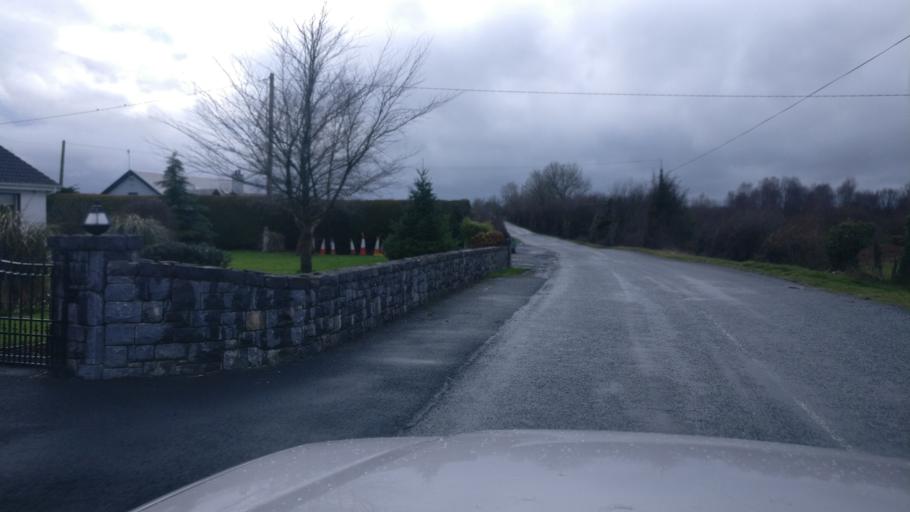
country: IE
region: Leinster
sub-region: An Iarmhi
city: Athlone
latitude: 53.4200
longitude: -8.0505
